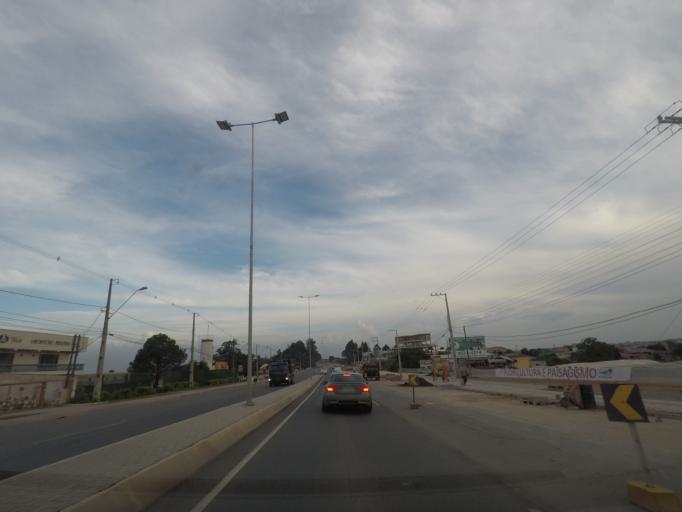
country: BR
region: Parana
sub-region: Colombo
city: Colombo
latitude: -25.3338
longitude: -49.2210
